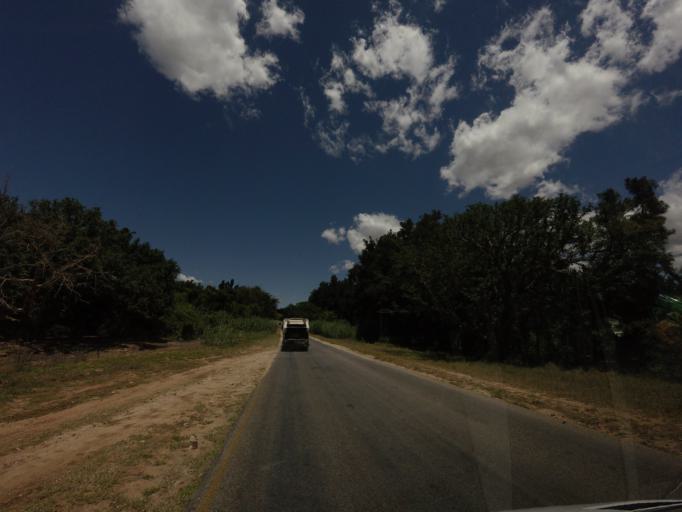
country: ZA
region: Limpopo
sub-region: Mopani District Municipality
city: Hoedspruit
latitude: -24.3892
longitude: 30.8424
